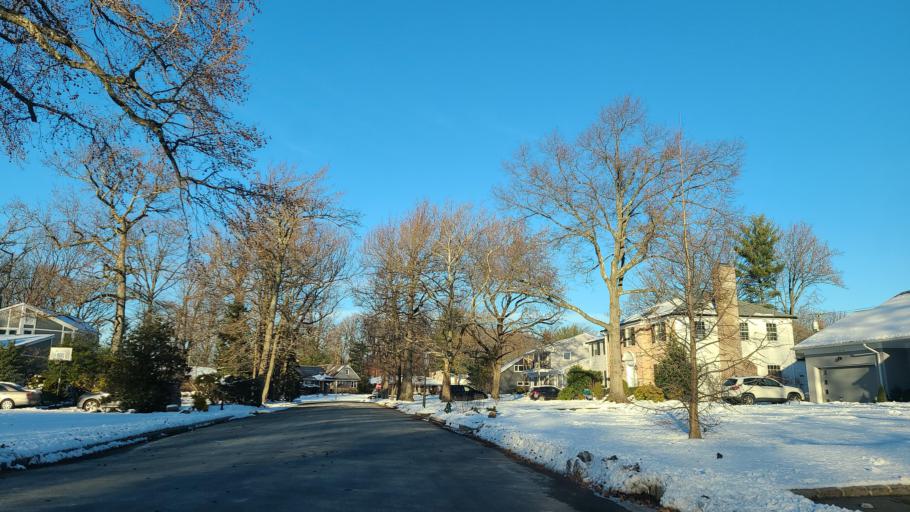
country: US
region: New Jersey
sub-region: Essex County
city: South Orange
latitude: 40.7595
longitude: -74.2728
